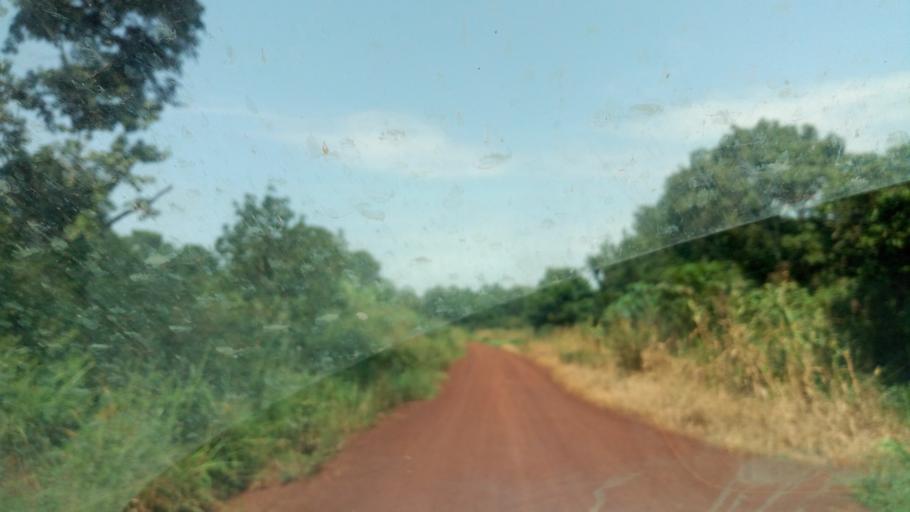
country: UG
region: Western Region
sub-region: Masindi District
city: Masindi
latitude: 1.6683
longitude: 31.8207
